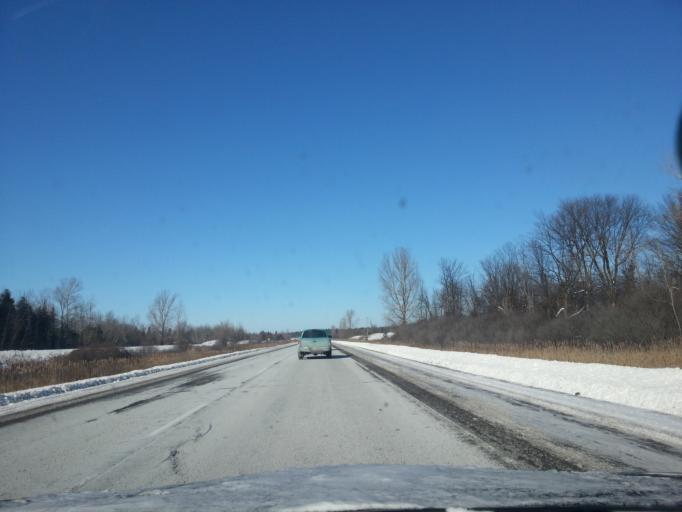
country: CA
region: Ontario
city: Bells Corners
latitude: 45.2832
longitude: -76.0024
